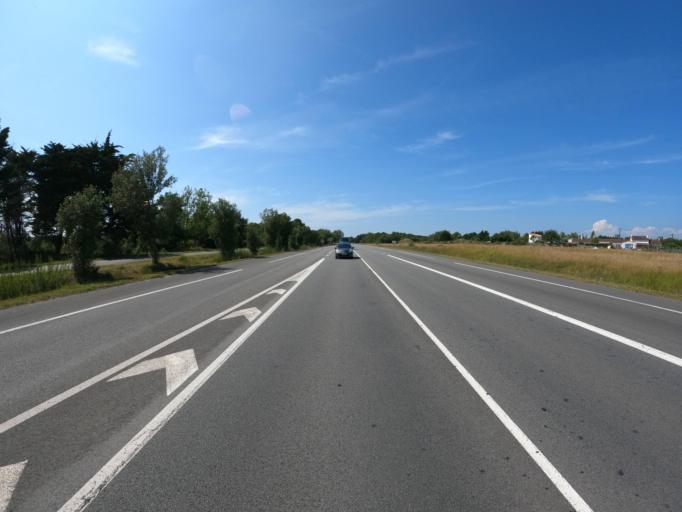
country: FR
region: Pays de la Loire
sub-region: Departement de la Loire-Atlantique
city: Les Moutiers-en-Retz
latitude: 47.0662
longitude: -1.9857
